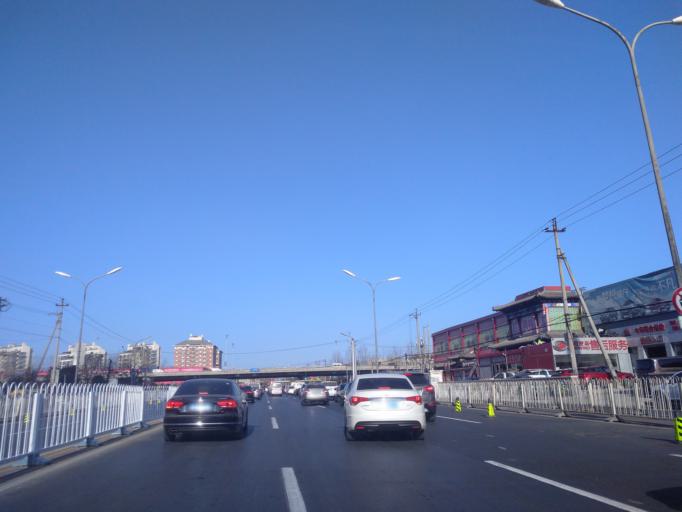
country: CN
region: Beijing
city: Jiugong
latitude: 39.8362
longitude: 116.4677
